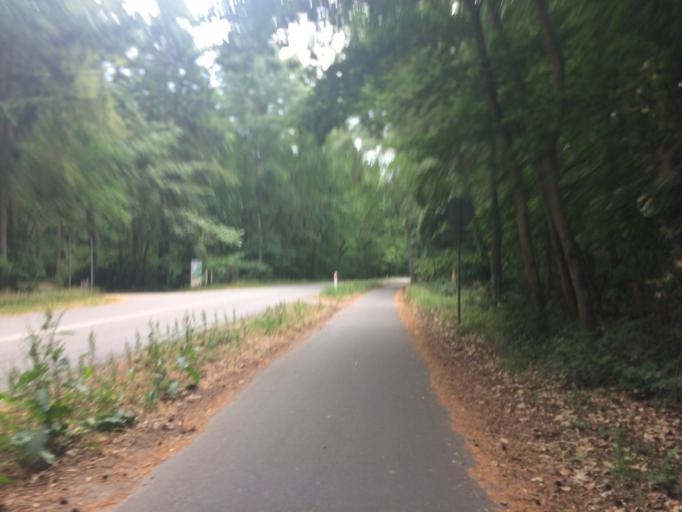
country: DK
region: Capital Region
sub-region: Bornholm Kommune
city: Ronne
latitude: 55.1657
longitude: 14.7153
